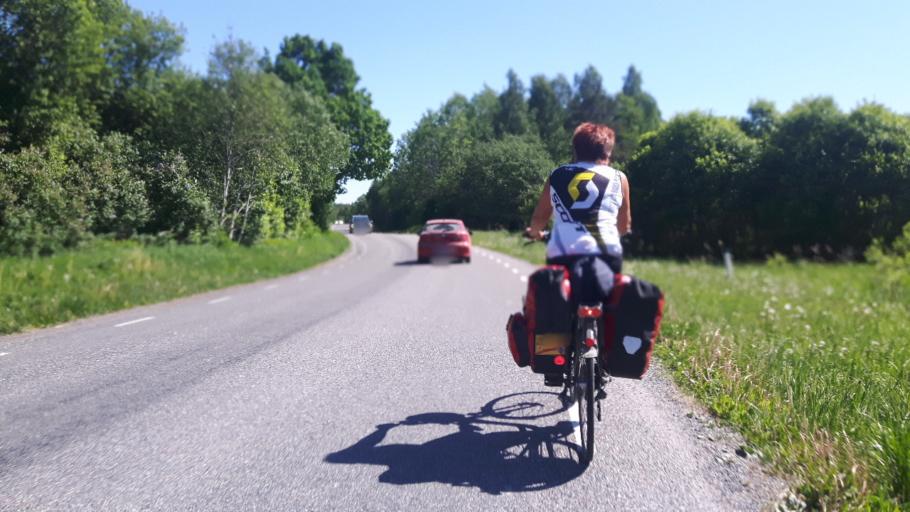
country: EE
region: Raplamaa
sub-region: Kohila vald
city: Kohila
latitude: 59.1823
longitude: 24.7186
